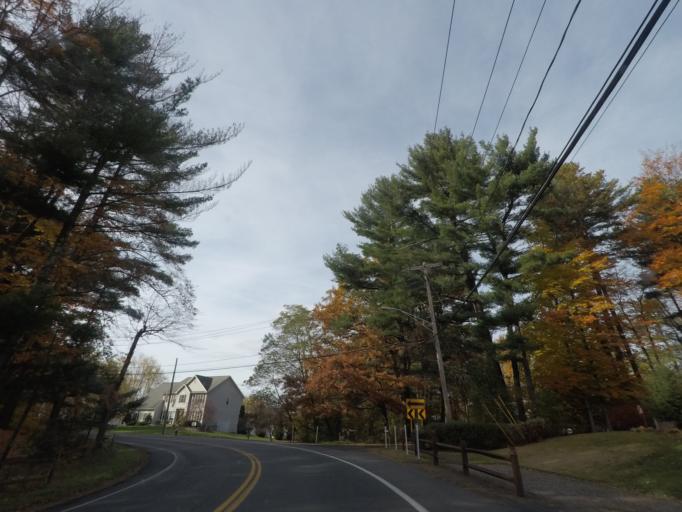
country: US
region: New York
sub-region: Schenectady County
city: Rotterdam
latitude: 42.7561
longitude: -73.9460
